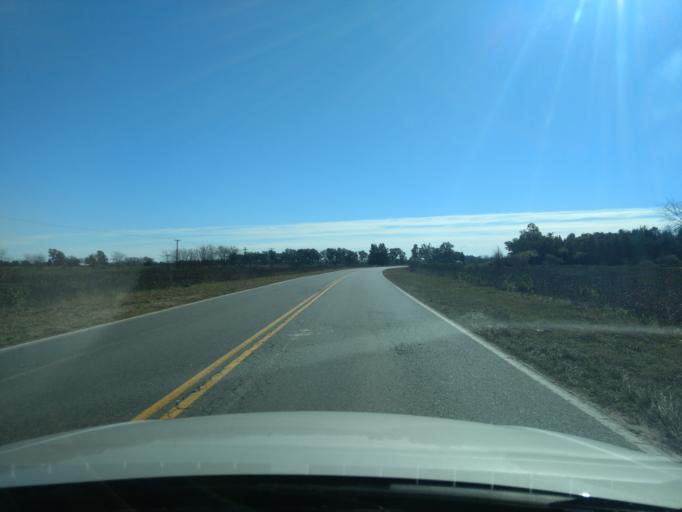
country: AR
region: Buenos Aires
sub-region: Partido de Lujan
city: Lujan
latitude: -34.6314
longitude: -59.1087
